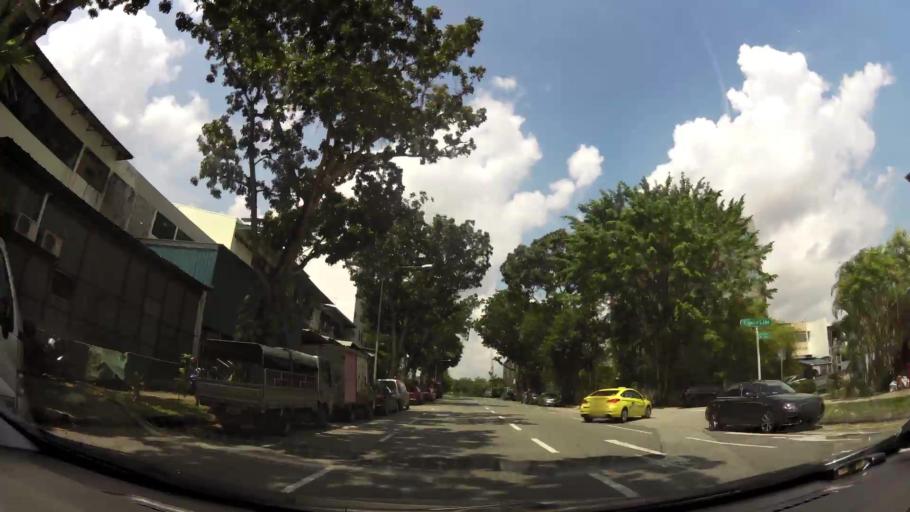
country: SG
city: Singapore
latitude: 1.3859
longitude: 103.8302
